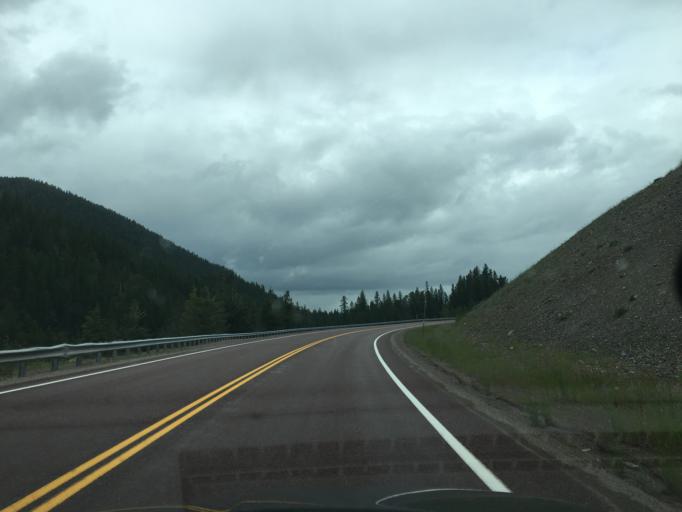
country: US
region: Montana
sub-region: Flathead County
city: Bigfork
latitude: 48.2362
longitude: -113.5688
